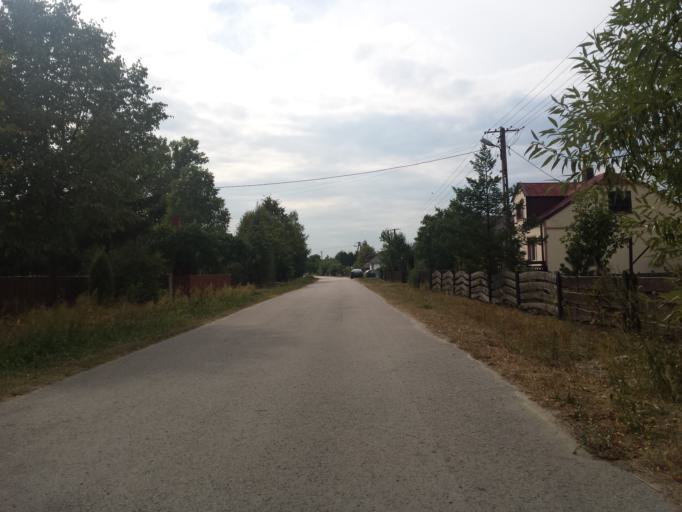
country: PL
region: Swietokrzyskie
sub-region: Powiat kielecki
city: Rakow
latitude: 50.6678
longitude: 21.1283
